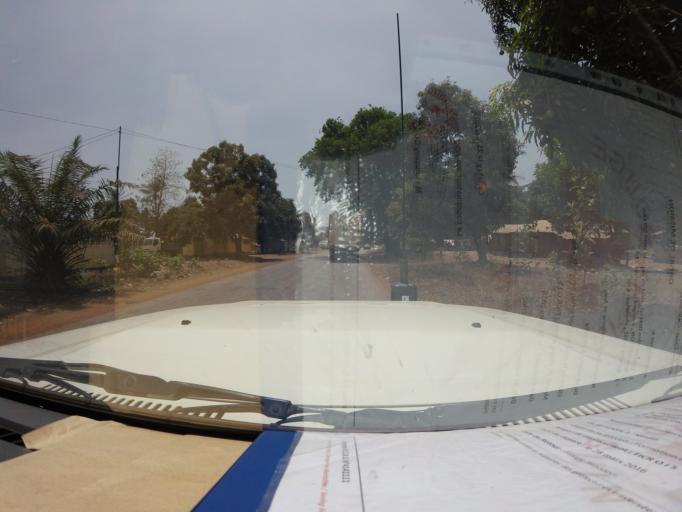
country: GN
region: Kindia
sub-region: Coyah
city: Coyah
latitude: 9.7943
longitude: -13.2965
